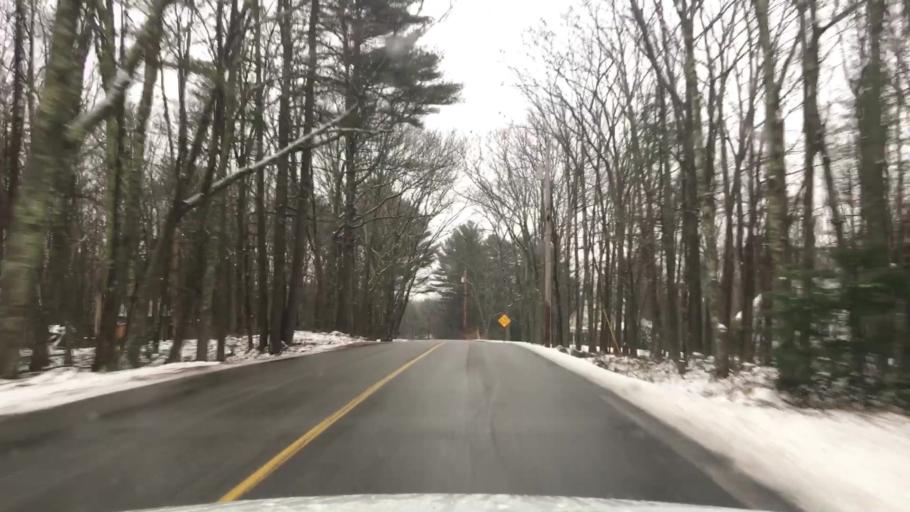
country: US
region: Maine
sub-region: York County
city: Arundel
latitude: 43.3754
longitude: -70.4601
